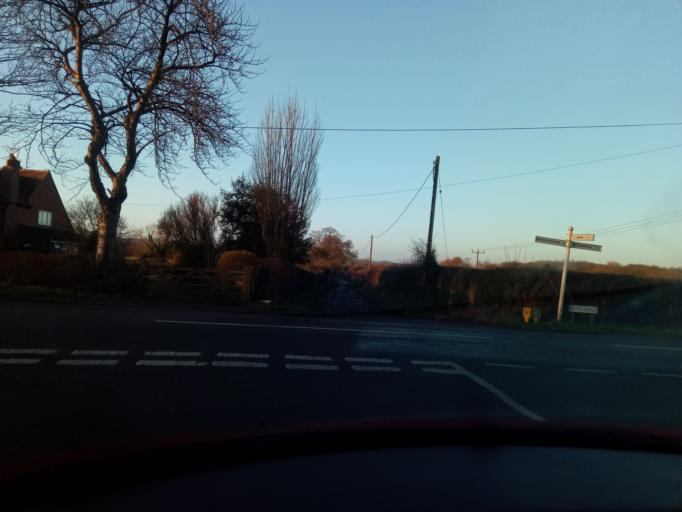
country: GB
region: England
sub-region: Leicestershire
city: Barrow upon Soar
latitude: 52.7714
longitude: -1.1623
